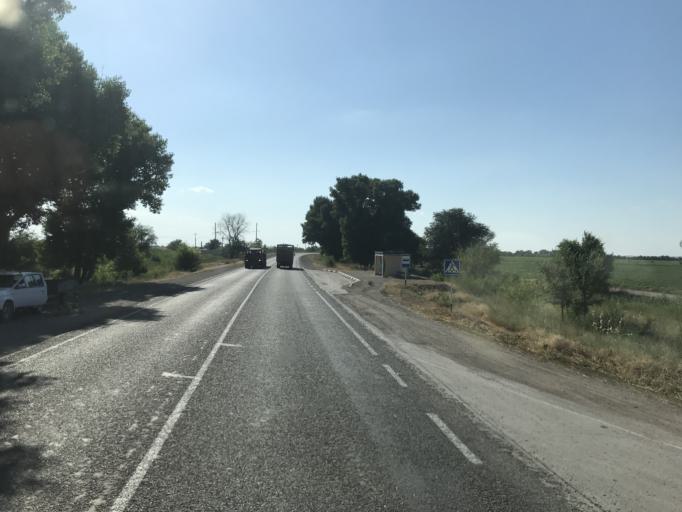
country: KZ
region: Zhambyl
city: Georgiyevka
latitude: 43.1898
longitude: 74.5445
